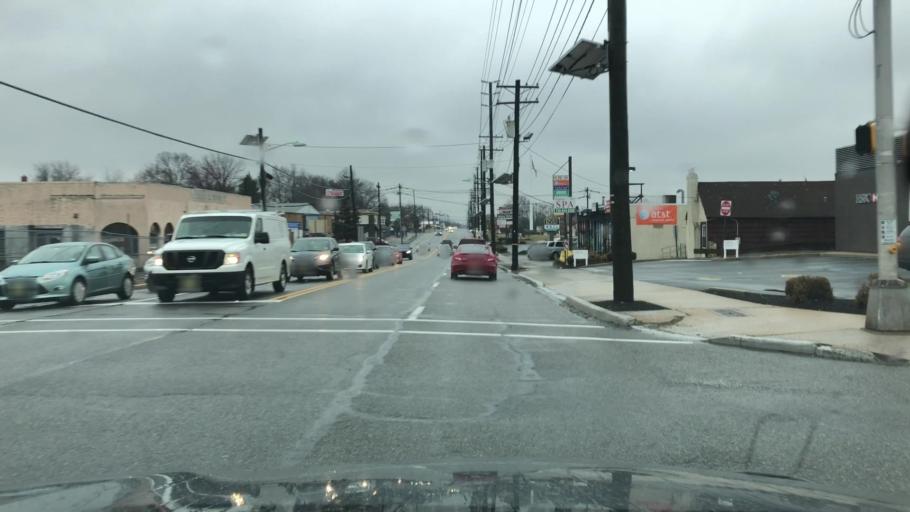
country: US
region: New Jersey
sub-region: Middlesex County
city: Edison
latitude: 40.5143
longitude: -74.4039
